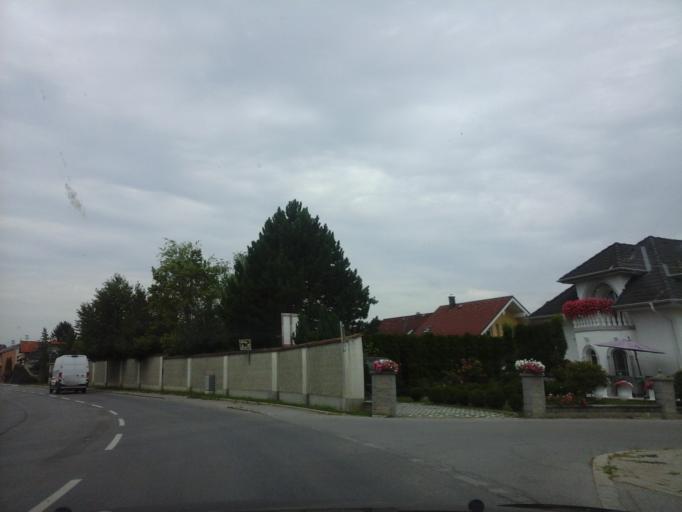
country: AT
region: Lower Austria
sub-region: Politischer Bezirk Ganserndorf
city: Orth an der Donau
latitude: 48.1474
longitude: 16.6992
